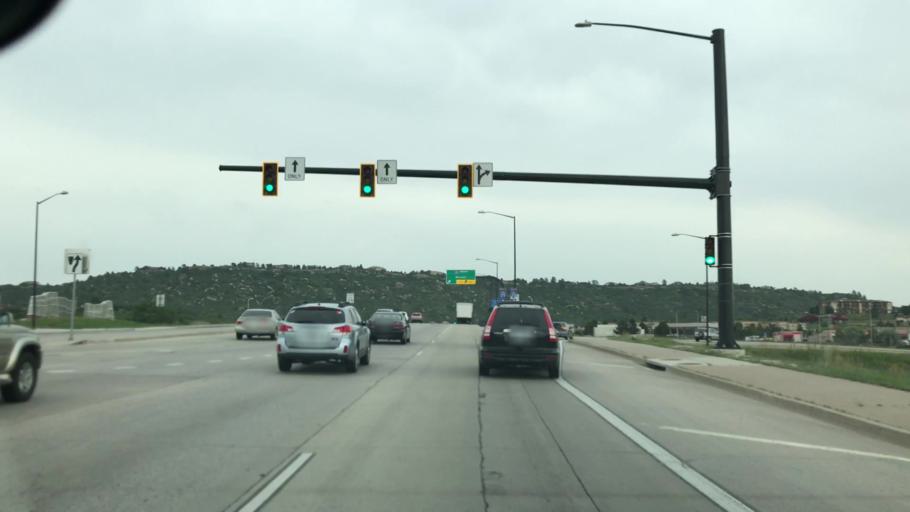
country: US
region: Colorado
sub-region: Douglas County
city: Castle Rock
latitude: 39.4118
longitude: -104.8699
